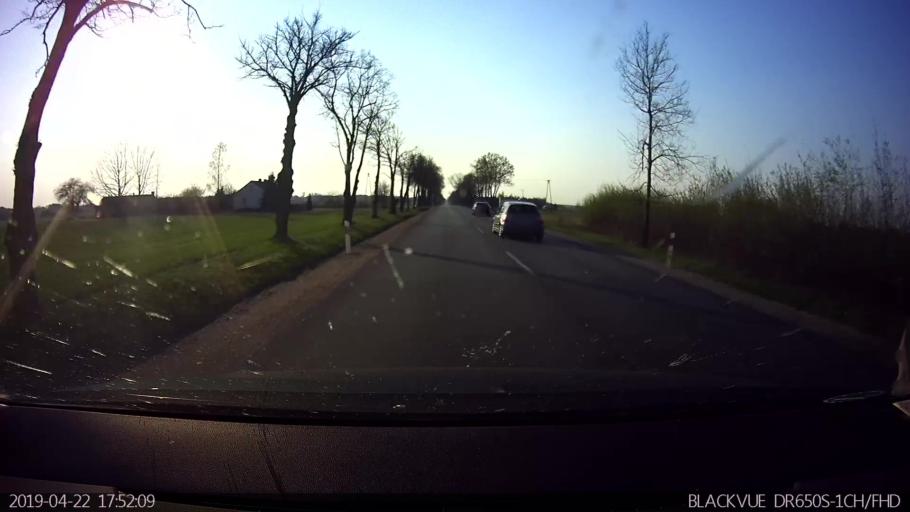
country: PL
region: Masovian Voivodeship
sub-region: Powiat wegrowski
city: Wegrow
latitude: 52.4398
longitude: 21.9833
